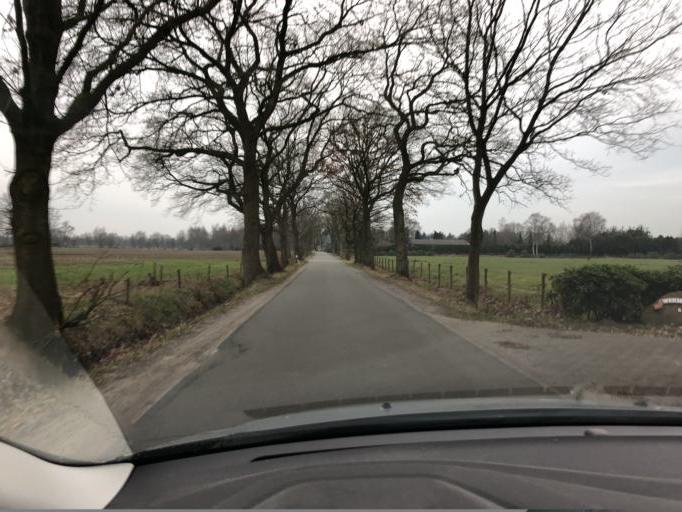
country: DE
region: Lower Saxony
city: Bad Zwischenahn
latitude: 53.1727
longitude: 8.0530
